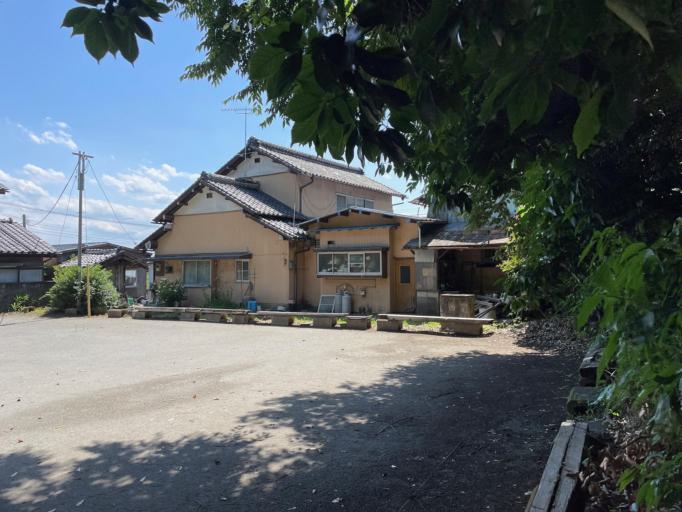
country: JP
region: Saitama
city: Sakado
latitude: 35.9982
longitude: 139.4119
